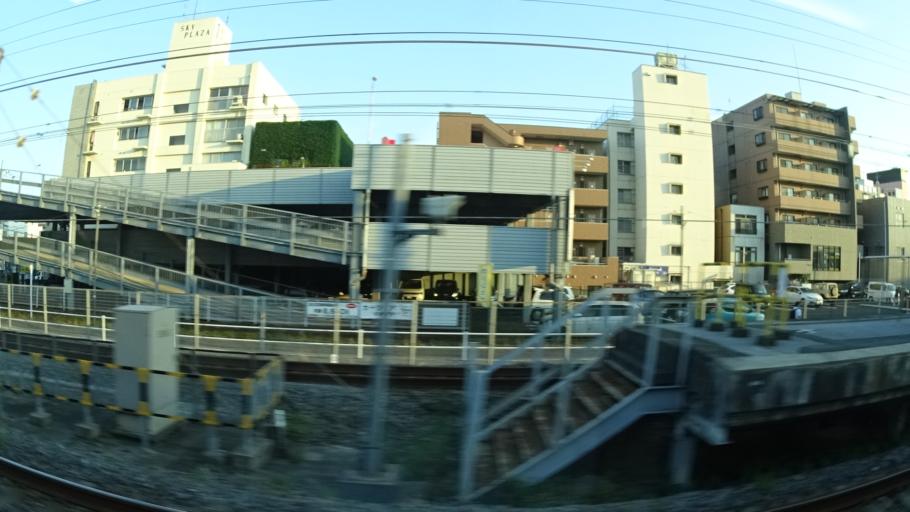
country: JP
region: Chiba
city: Abiko
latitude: 35.8725
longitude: 140.0424
